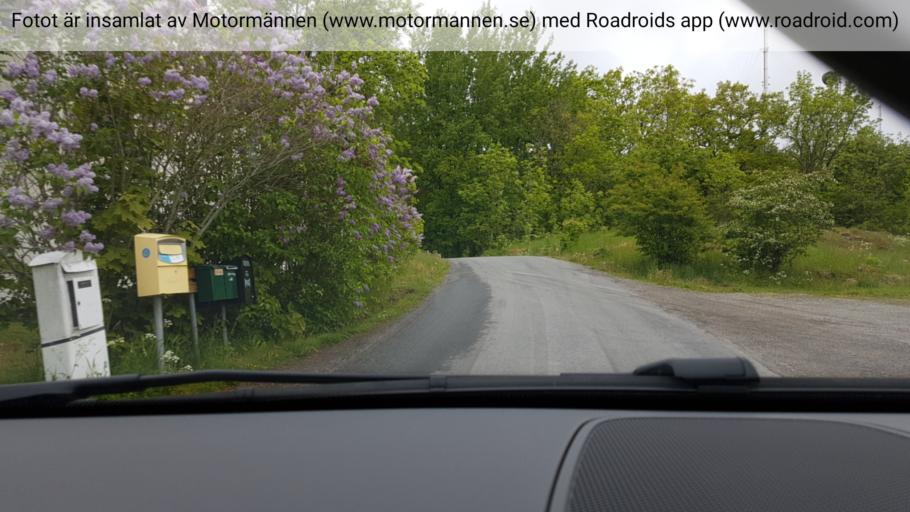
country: SE
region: Stockholm
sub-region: Haninge Kommun
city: Jordbro
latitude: 59.0077
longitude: 18.1231
